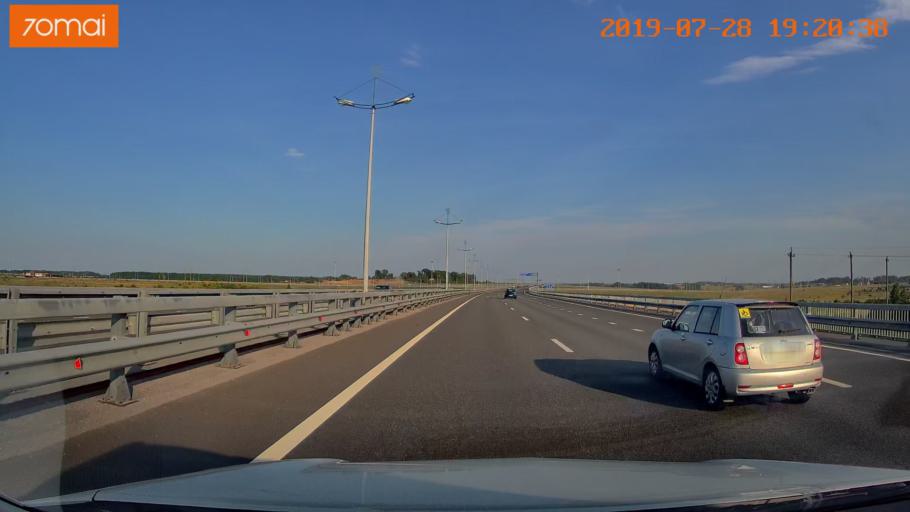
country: RU
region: Kaliningrad
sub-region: Zelenogradskiy Rayon
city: Zelenogradsk
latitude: 54.9135
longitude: 20.4907
